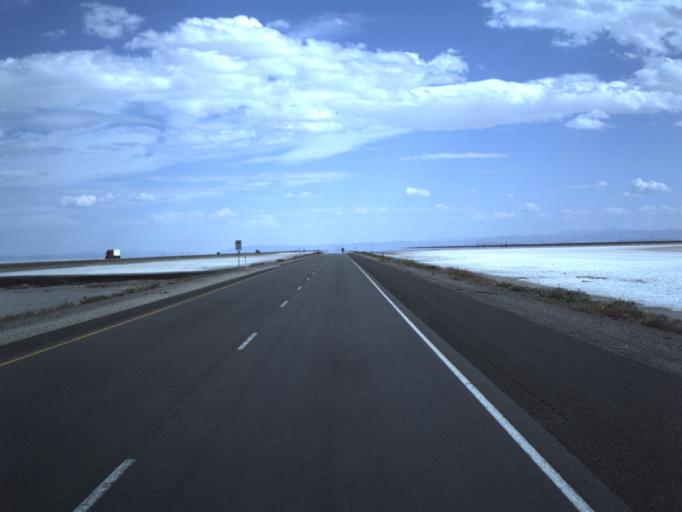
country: US
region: Utah
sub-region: Tooele County
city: Wendover
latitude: 40.7352
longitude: -113.6909
